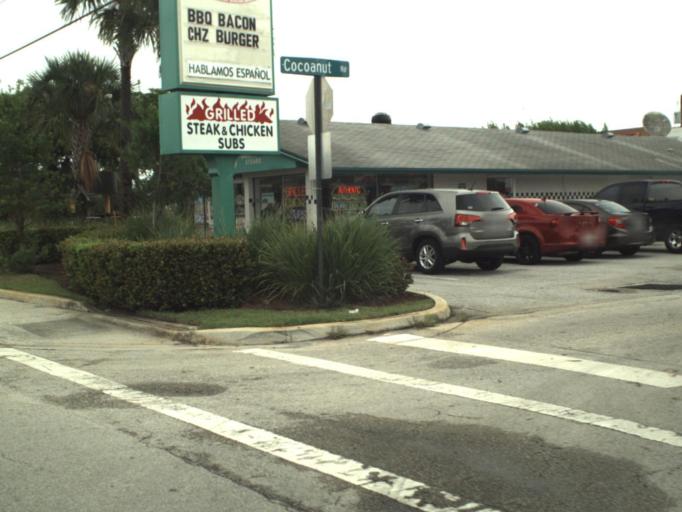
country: US
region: Florida
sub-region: Palm Beach County
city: Royal Palm Estates
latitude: 26.6616
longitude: -80.1125
